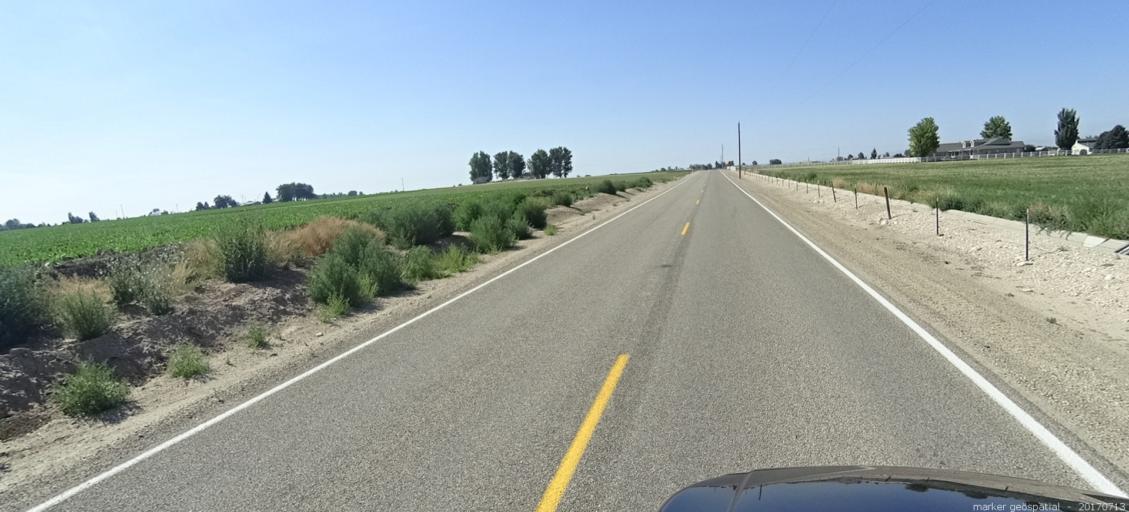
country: US
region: Idaho
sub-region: Ada County
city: Kuna
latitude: 43.5063
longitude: -116.3743
